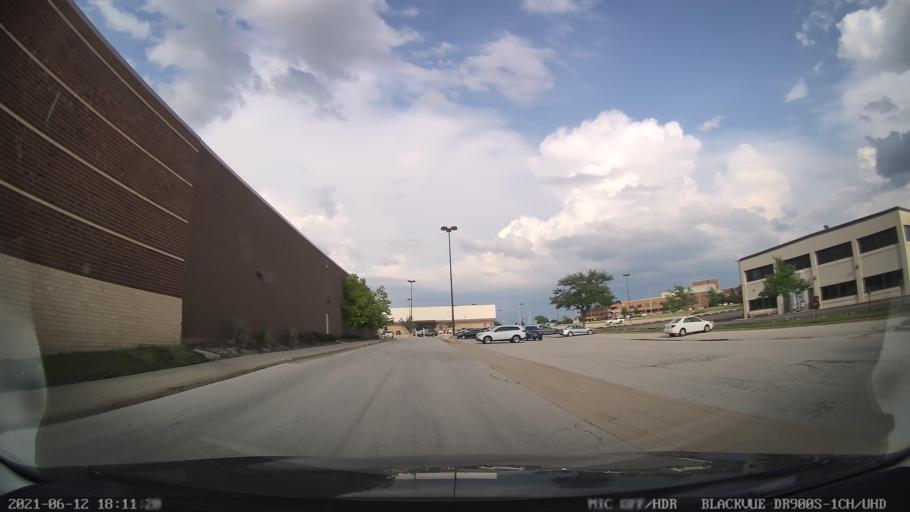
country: US
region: Illinois
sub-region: McLean County
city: Bloomington
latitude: 40.4848
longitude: -88.9584
